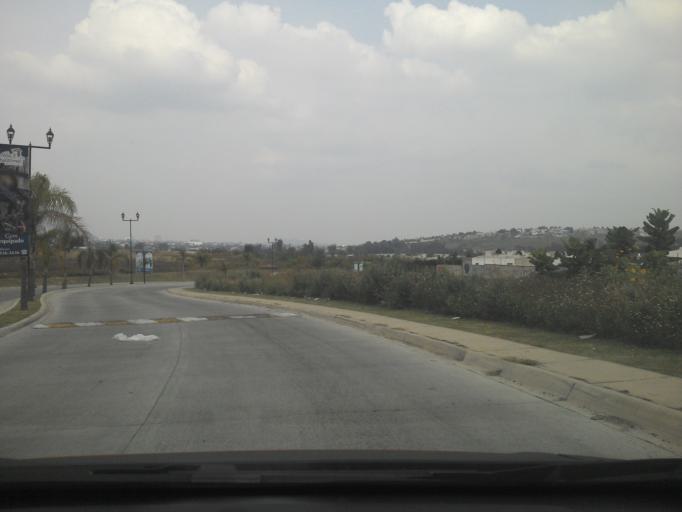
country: MX
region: Jalisco
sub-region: Tlajomulco de Zuniga
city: Lomas de San Agustin
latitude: 20.5299
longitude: -103.4737
